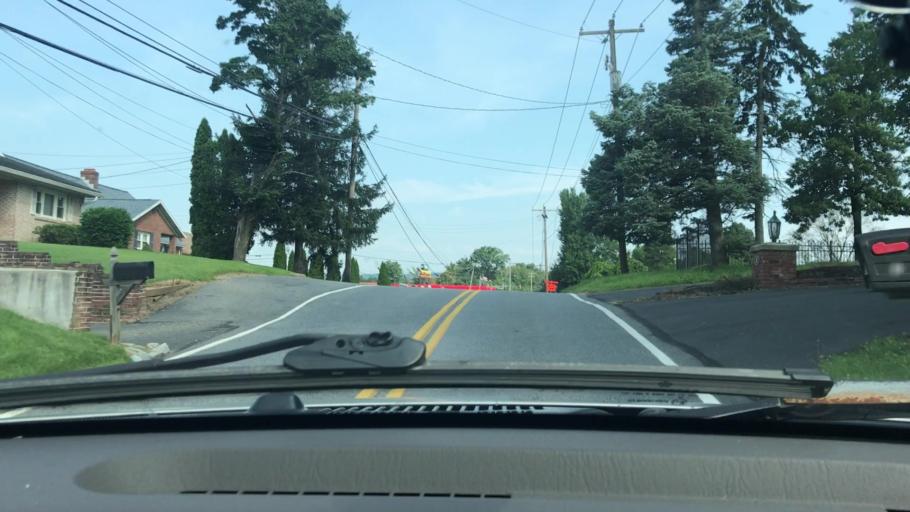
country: US
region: Pennsylvania
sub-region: Dauphin County
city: Linglestown
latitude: 40.3227
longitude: -76.7801
